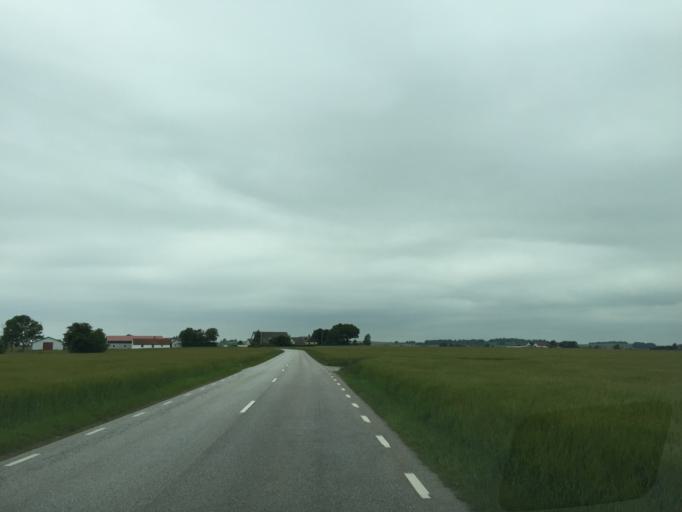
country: SE
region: Skane
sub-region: Ystads Kommun
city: Kopingebro
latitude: 55.4352
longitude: 14.0232
